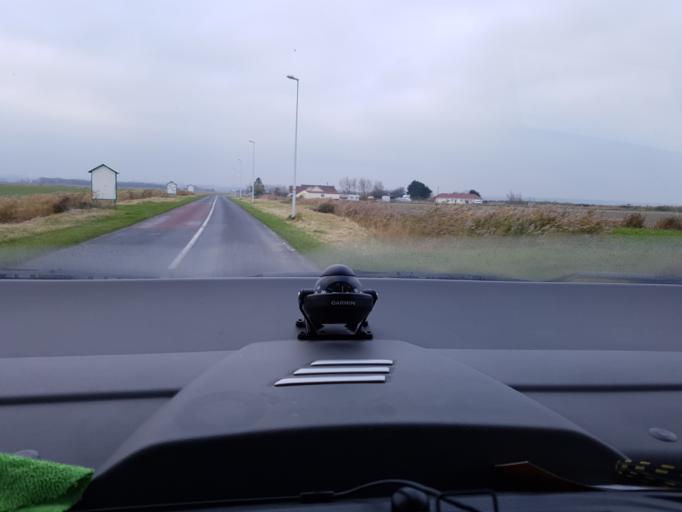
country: FR
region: Picardie
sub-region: Departement de la Somme
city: Cayeux-sur-Mer
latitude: 50.1676
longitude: 1.4939
